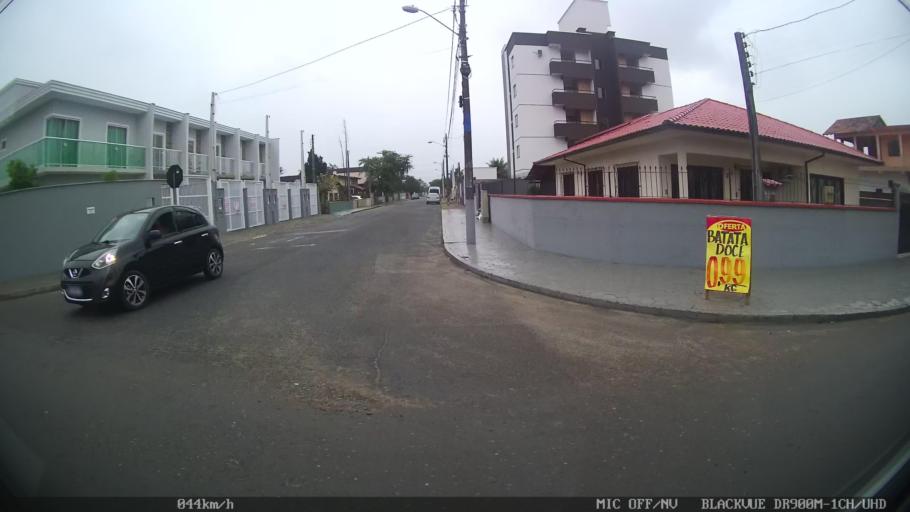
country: BR
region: Santa Catarina
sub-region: Joinville
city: Joinville
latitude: -26.2745
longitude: -48.8042
